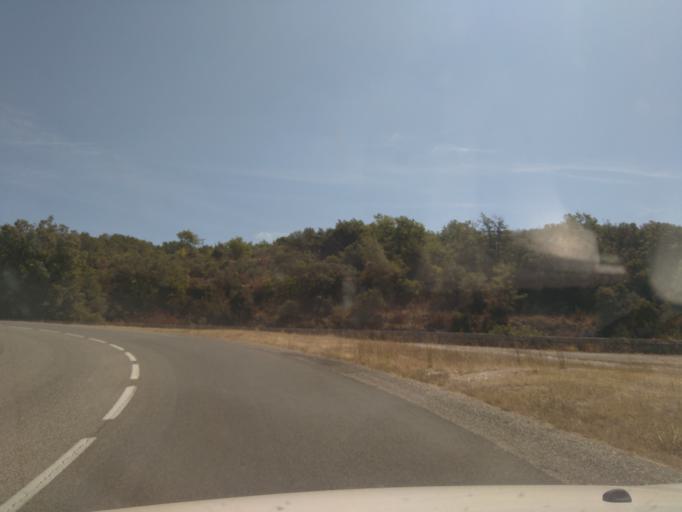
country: FR
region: Provence-Alpes-Cote d'Azur
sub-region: Departement du Var
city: Regusse
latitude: 43.7101
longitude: 6.0444
